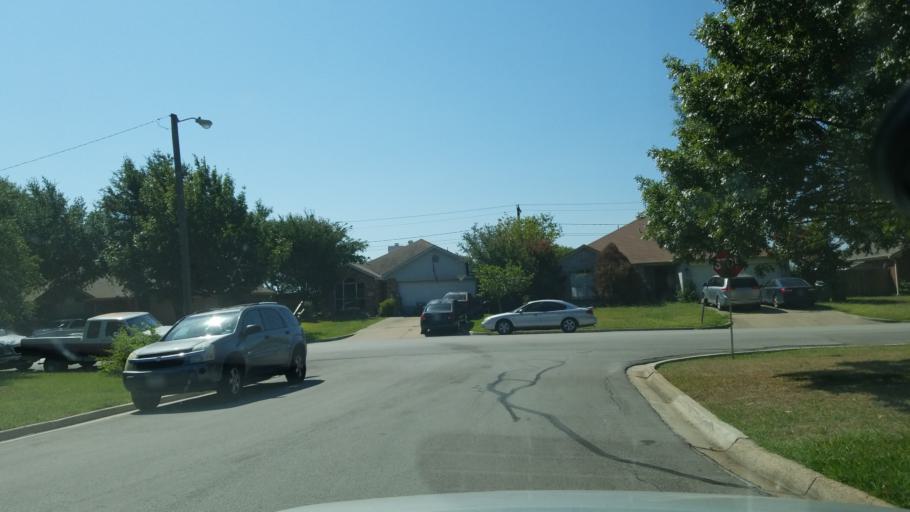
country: US
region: Texas
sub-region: Tarrant County
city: Mansfield
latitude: 32.5538
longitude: -97.1325
